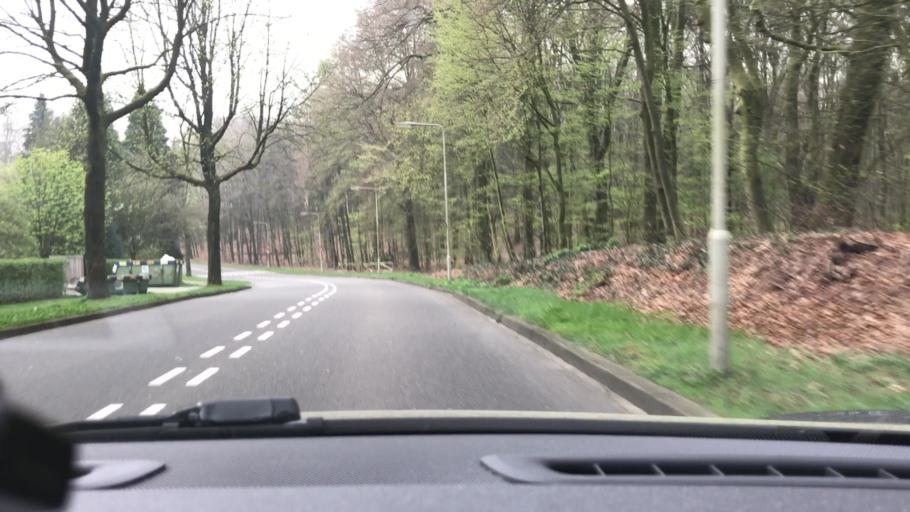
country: NL
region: Gelderland
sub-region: Gemeente Arnhem
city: Arnhem
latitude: 51.9987
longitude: 5.9303
